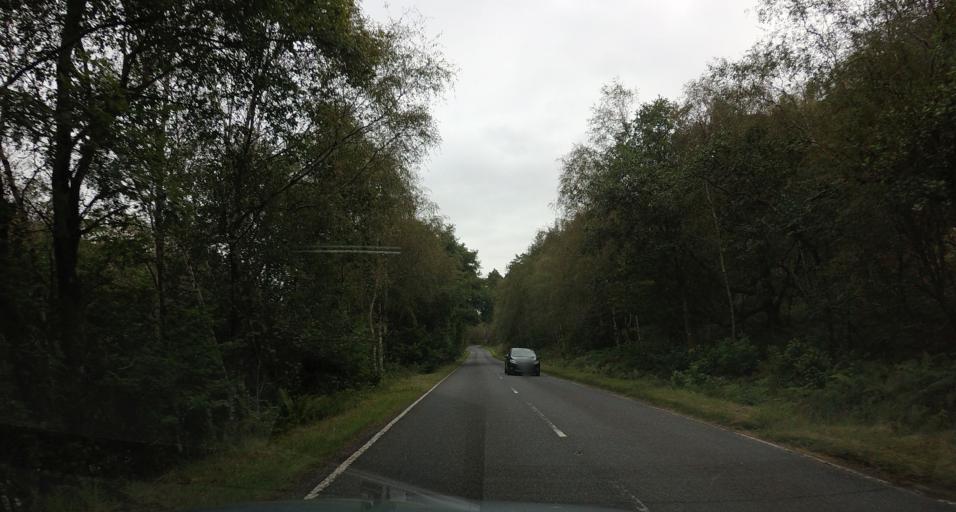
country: GB
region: Scotland
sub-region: Highland
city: Fort William
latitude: 56.6937
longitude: -5.0963
